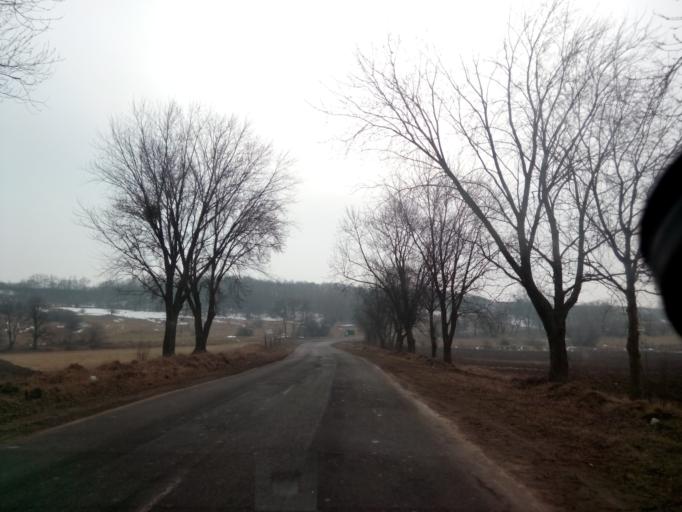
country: HU
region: Borsod-Abauj-Zemplen
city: Gonc
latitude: 48.4818
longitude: 21.2561
